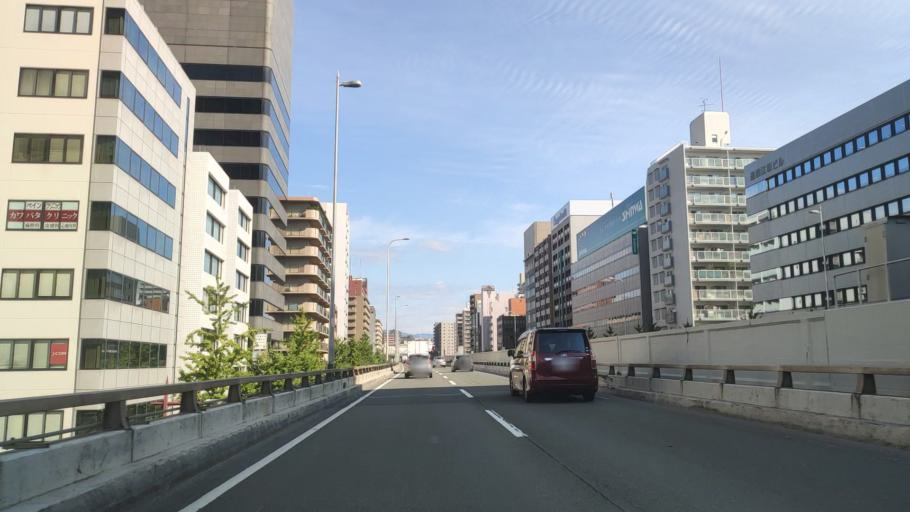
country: JP
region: Osaka
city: Suita
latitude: 34.7596
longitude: 135.4970
